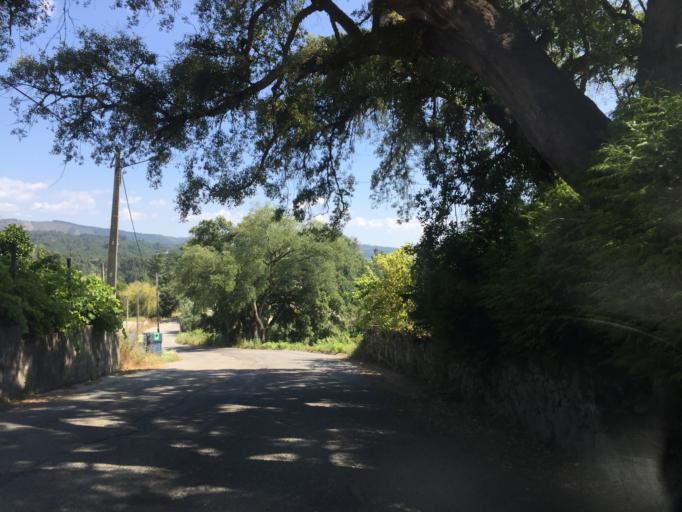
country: PT
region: Leiria
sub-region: Pedrogao Grande
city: Pedrogao Grande
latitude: 39.9075
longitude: -8.1443
